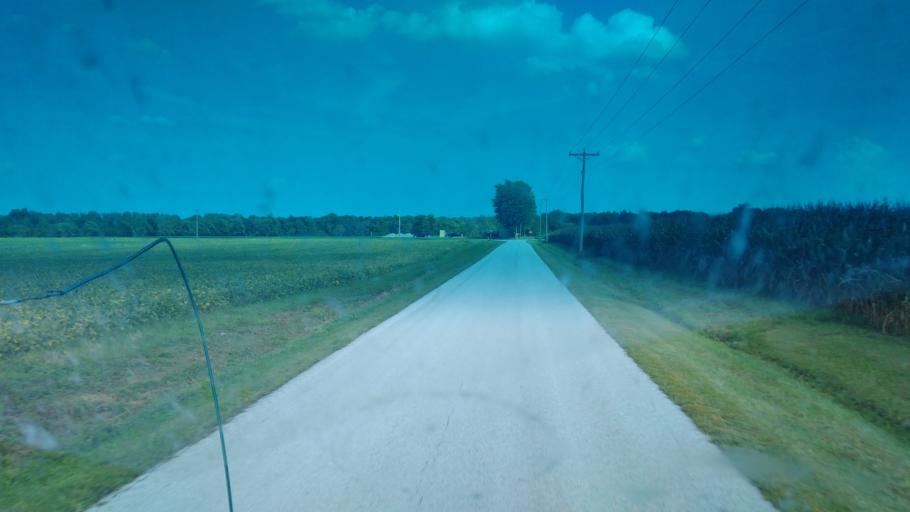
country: US
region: Ohio
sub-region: Hancock County
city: Arlington
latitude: 40.8769
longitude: -83.5734
